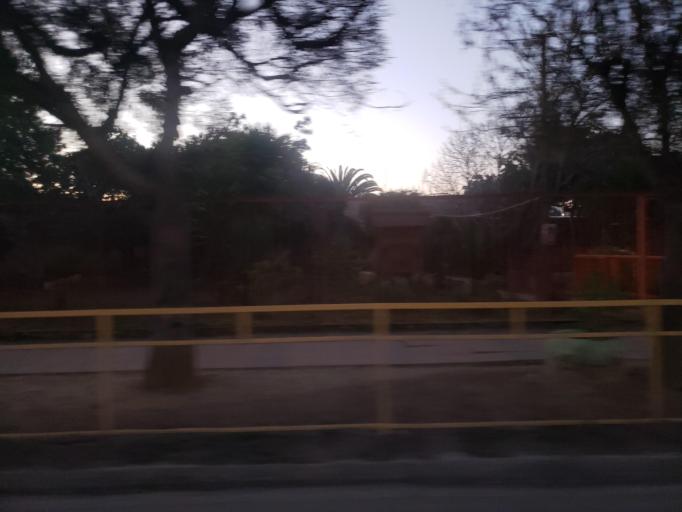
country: CL
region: Santiago Metropolitan
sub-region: Provincia de Talagante
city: El Monte
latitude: -33.6835
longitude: -70.9979
